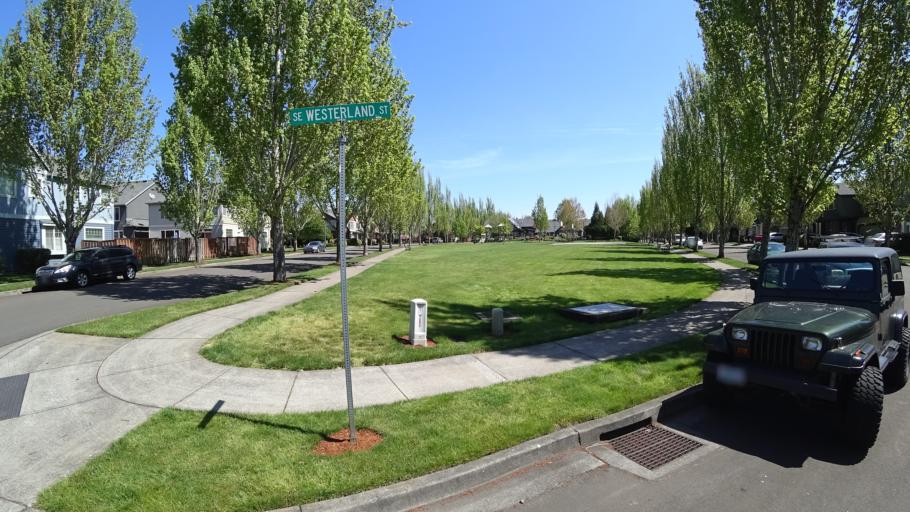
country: US
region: Oregon
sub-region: Washington County
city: Hillsboro
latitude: 45.5082
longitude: -122.9755
